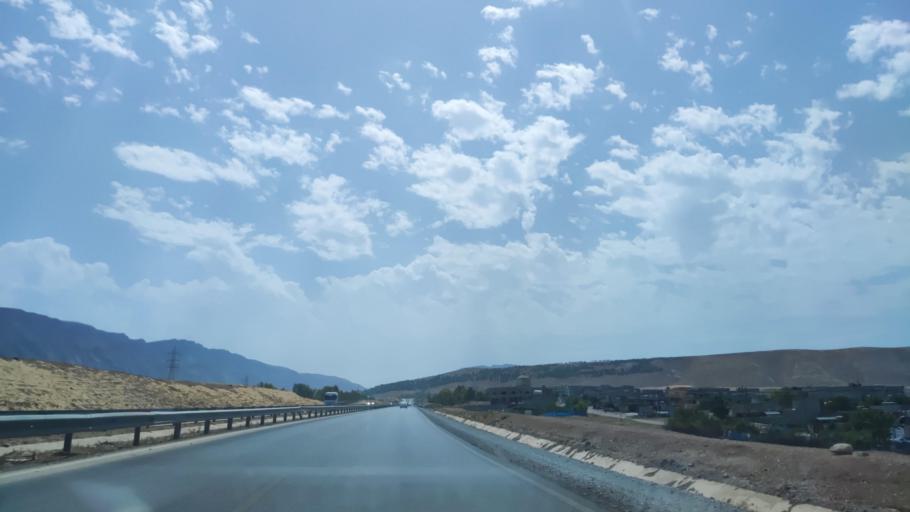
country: IQ
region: Arbil
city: Shaqlawah
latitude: 36.5047
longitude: 44.3524
